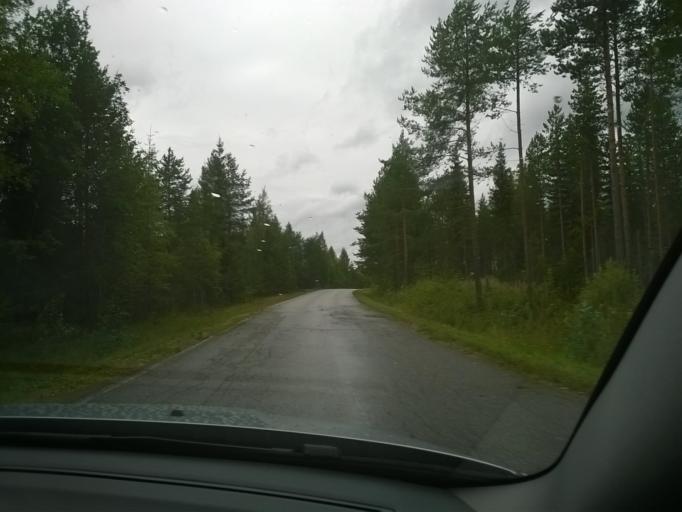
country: FI
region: Kainuu
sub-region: Kehys-Kainuu
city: Kuhmo
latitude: 64.1278
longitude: 29.4620
